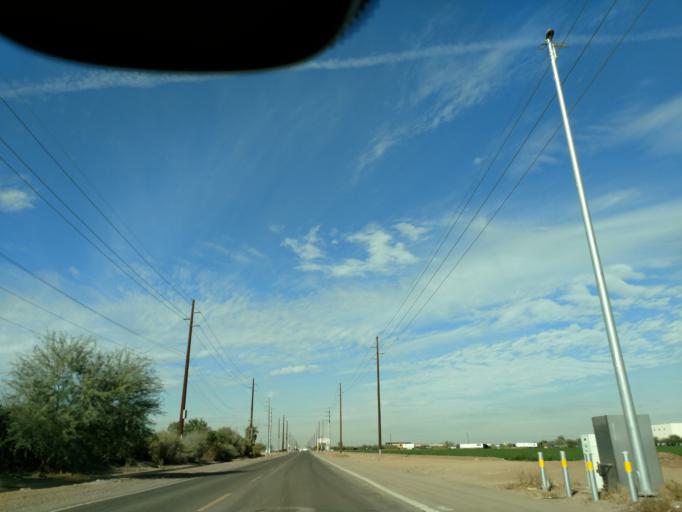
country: US
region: Arizona
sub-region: Maricopa County
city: Laveen
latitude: 33.4186
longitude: -112.1865
